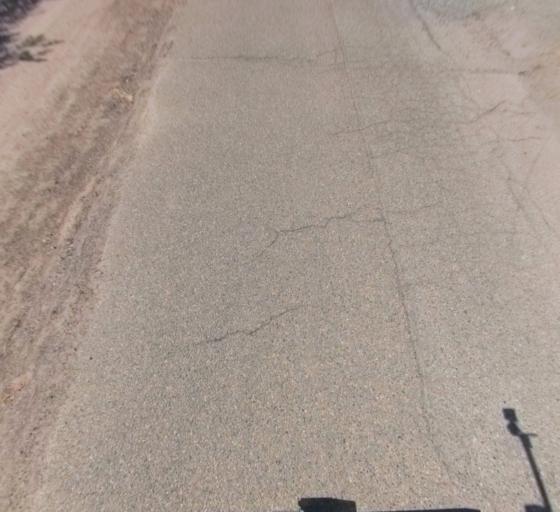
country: US
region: California
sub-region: Madera County
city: Parksdale
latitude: 36.9286
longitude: -119.9396
